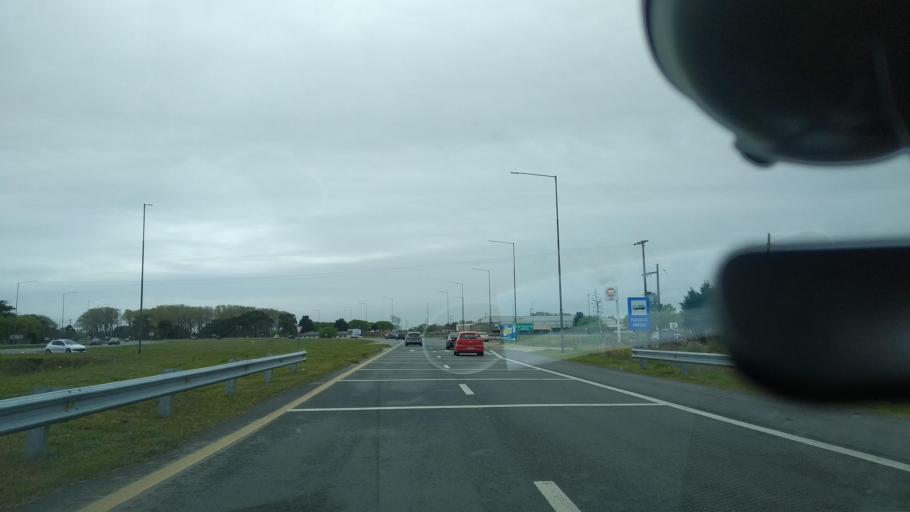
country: AR
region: Buenos Aires
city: Mar del Tuyu
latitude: -36.4907
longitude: -56.7117
